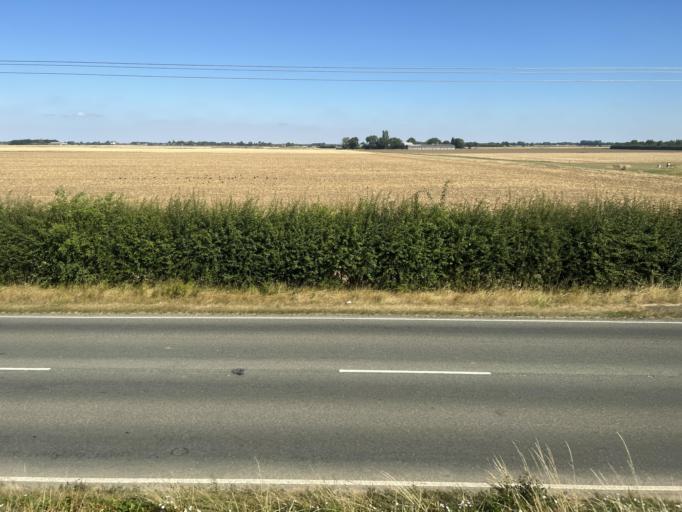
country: GB
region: England
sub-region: Lincolnshire
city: Kirton
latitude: 52.9734
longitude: -0.0774
